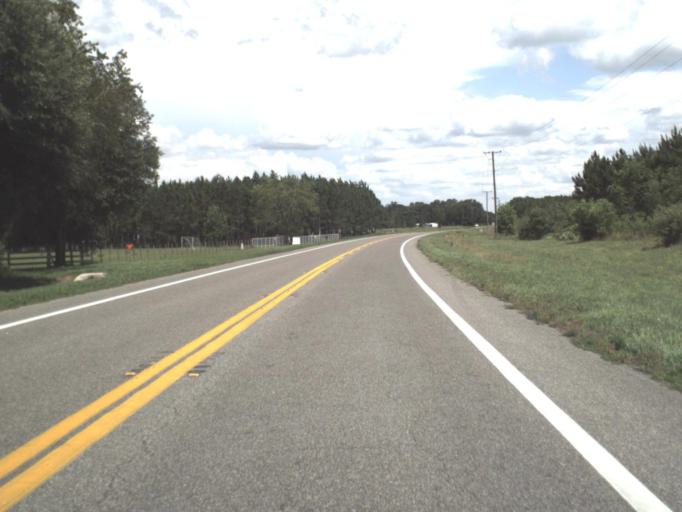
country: US
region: Florida
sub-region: Lafayette County
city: Mayo
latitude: 30.0510
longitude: -83.0870
